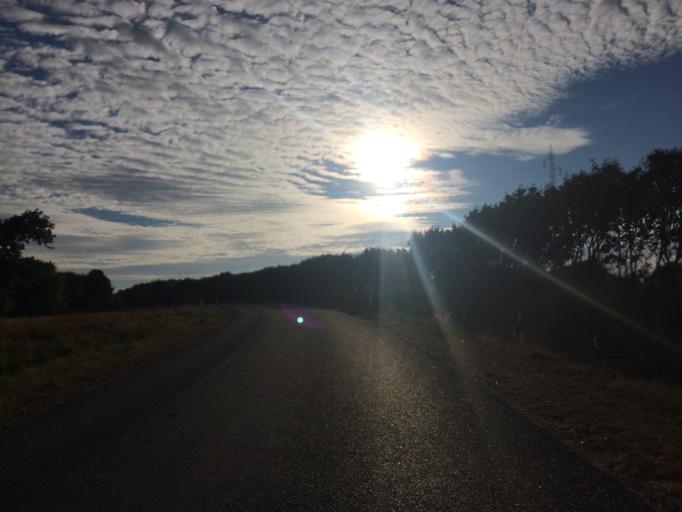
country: DK
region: Central Jutland
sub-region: Holstebro Kommune
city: Vinderup
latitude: 56.5862
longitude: 8.8195
